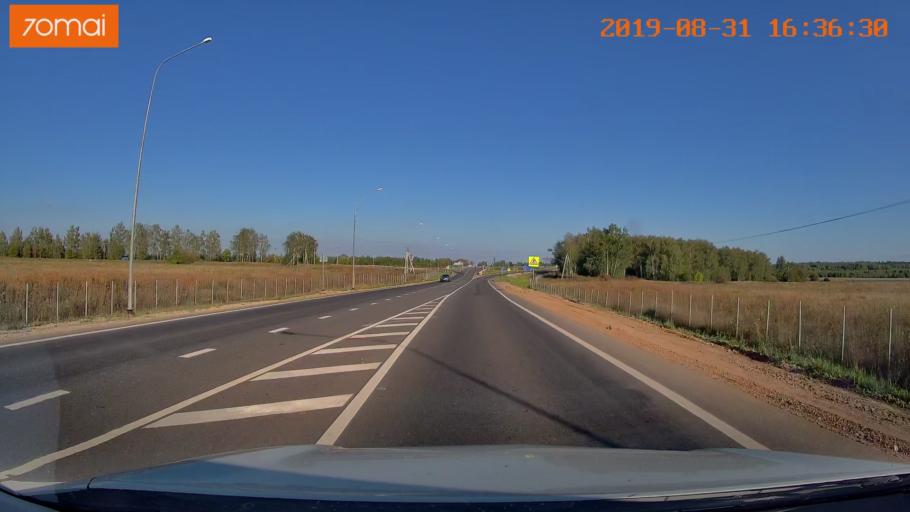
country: RU
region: Kaluga
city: Kurovskoye
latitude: 54.5287
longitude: 35.9757
